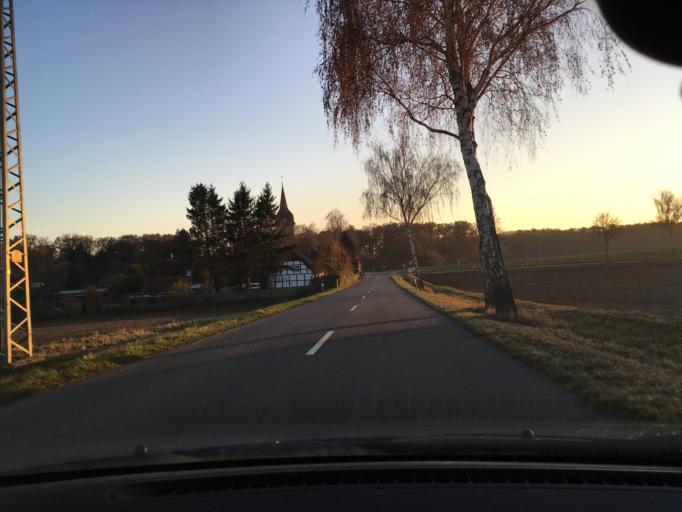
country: DE
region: Lower Saxony
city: Natendorf
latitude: 53.0830
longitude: 10.4658
